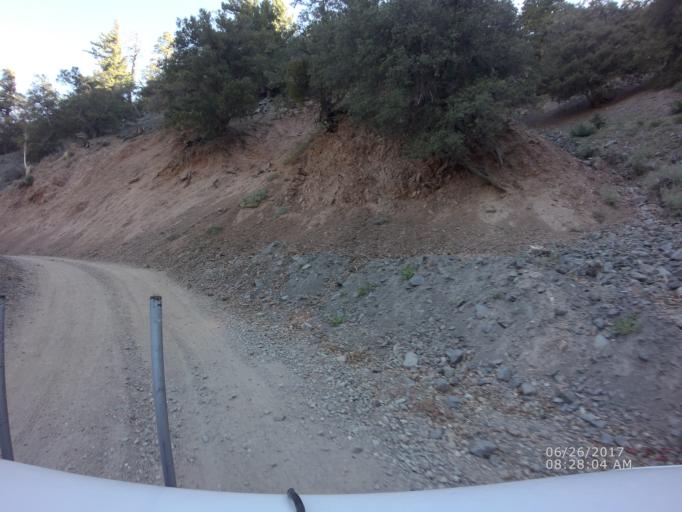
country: US
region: California
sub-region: San Bernardino County
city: Wrightwood
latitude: 34.3757
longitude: -117.7542
